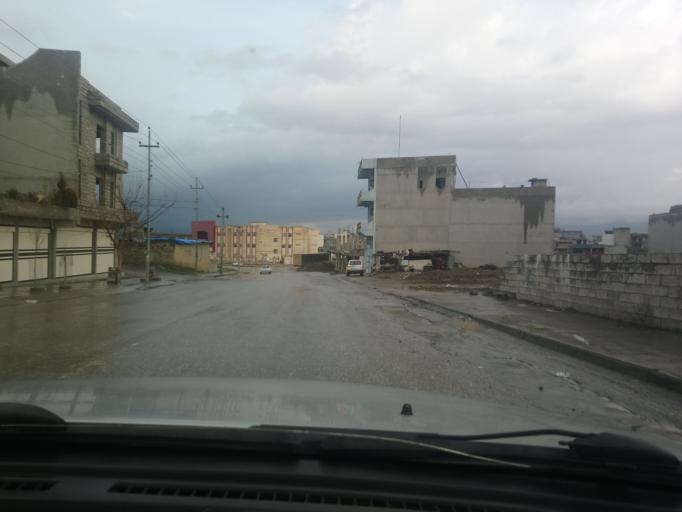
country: IQ
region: As Sulaymaniyah
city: Qeladize
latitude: 36.1803
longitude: 45.1377
